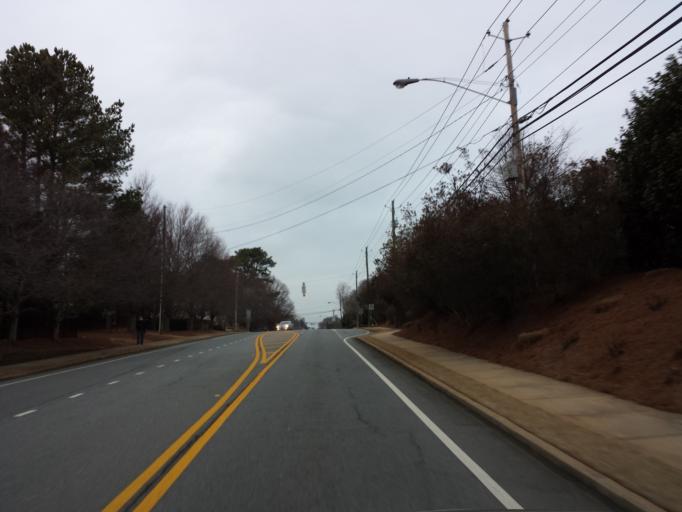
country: US
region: Georgia
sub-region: Fulton County
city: Roswell
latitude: 34.0433
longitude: -84.3612
